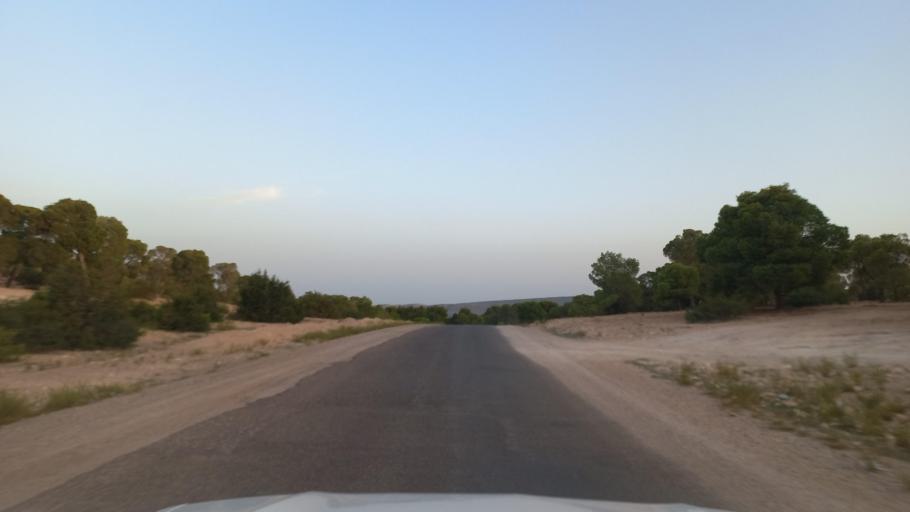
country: TN
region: Al Qasrayn
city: Sbiba
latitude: 35.4249
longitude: 8.9214
